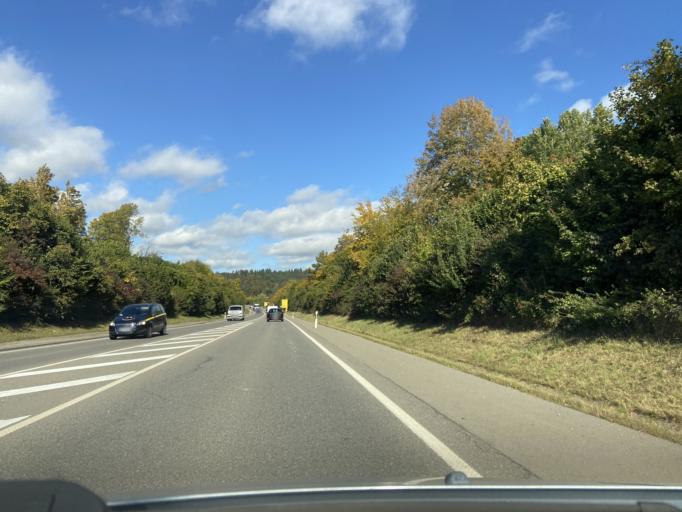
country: DE
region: Baden-Wuerttemberg
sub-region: Tuebingen Region
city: Sigmaringen
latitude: 48.0816
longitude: 9.2066
